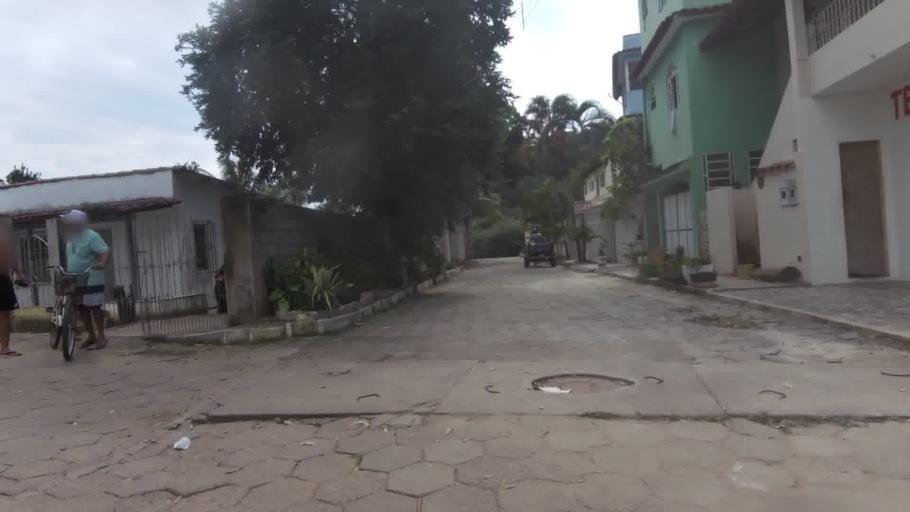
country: BR
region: Espirito Santo
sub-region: Piuma
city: Piuma
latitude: -20.8403
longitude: -40.7414
